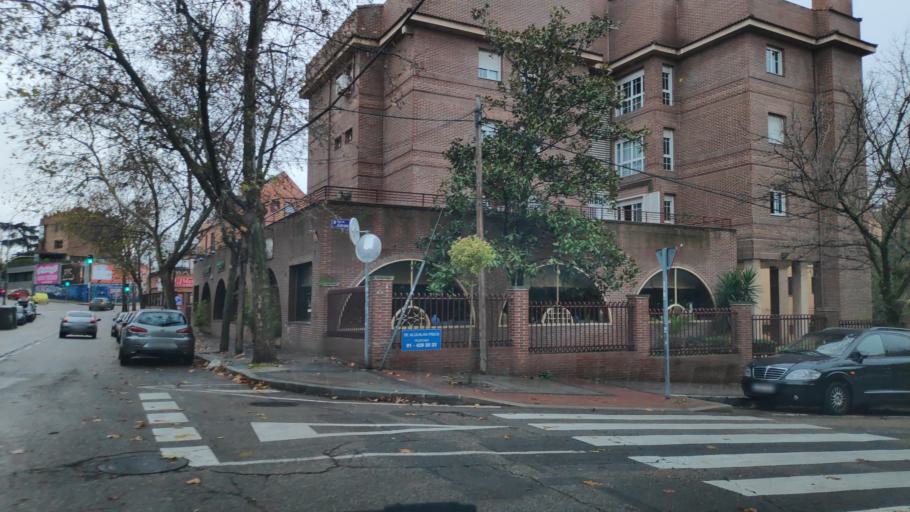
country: ES
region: Madrid
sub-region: Provincia de Madrid
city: Chamartin
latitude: 40.4642
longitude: -3.6626
